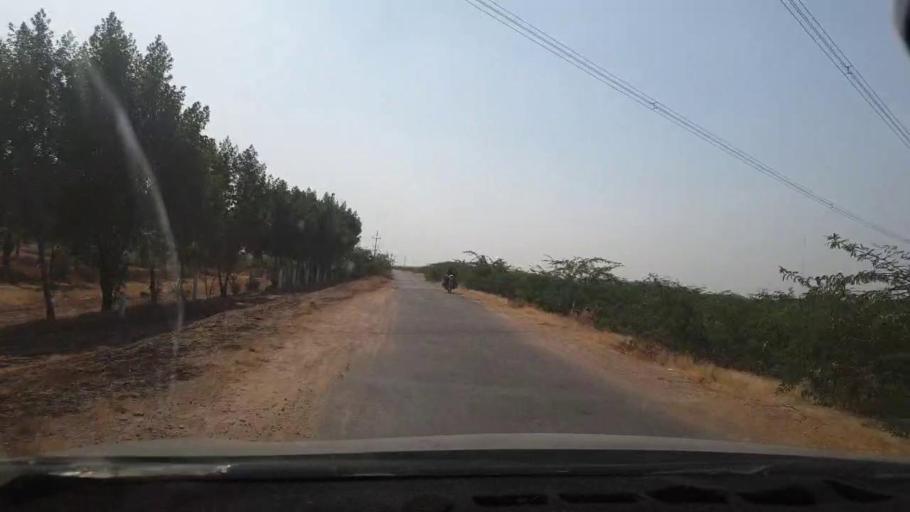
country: PK
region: Sindh
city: Malir Cantonment
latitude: 25.1107
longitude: 67.2047
